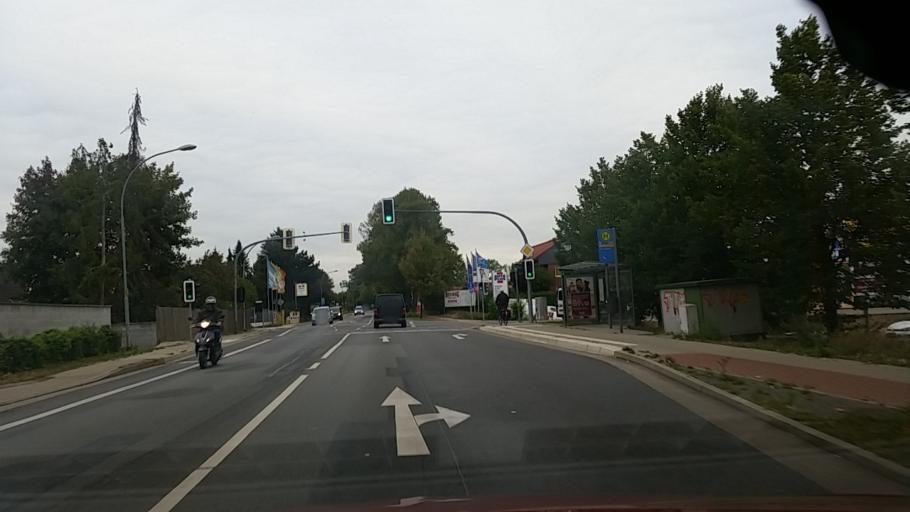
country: DE
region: Lower Saxony
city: Gifhorn
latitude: 52.4990
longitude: 10.5419
